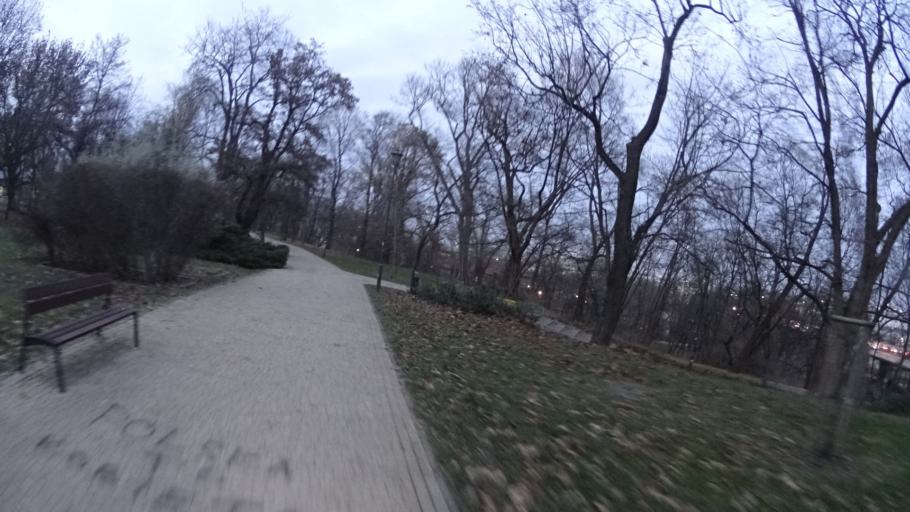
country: PL
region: Masovian Voivodeship
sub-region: Warszawa
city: Srodmiescie
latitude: 52.2213
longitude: 21.0308
